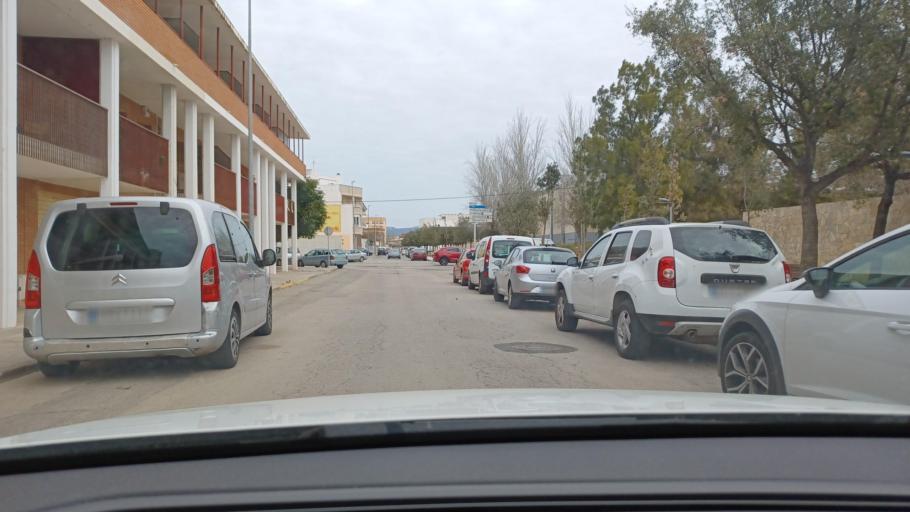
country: ES
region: Catalonia
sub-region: Provincia de Tarragona
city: Amposta
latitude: 40.7054
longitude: 0.5819
